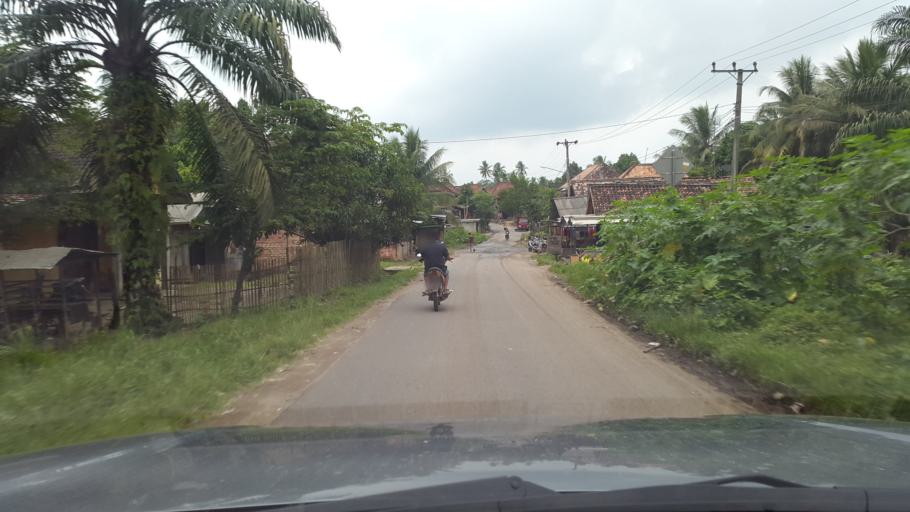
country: ID
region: South Sumatra
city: Gunungmenang
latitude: -3.2553
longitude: 104.0591
